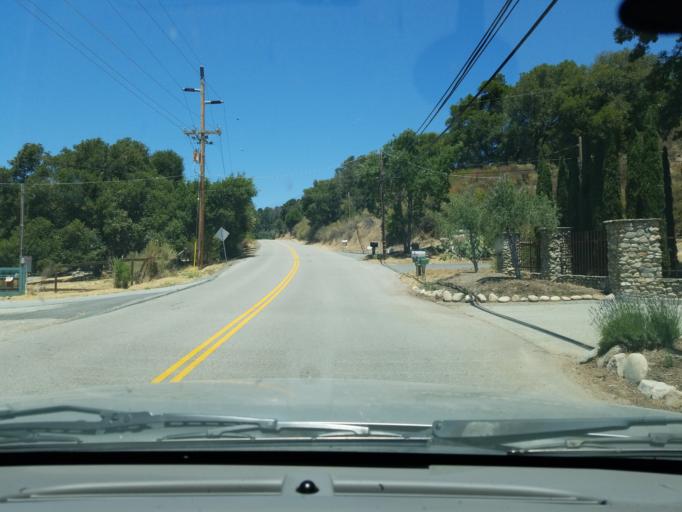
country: US
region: California
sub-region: Monterey County
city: Carmel Valley Village
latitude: 36.4726
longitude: -121.7172
